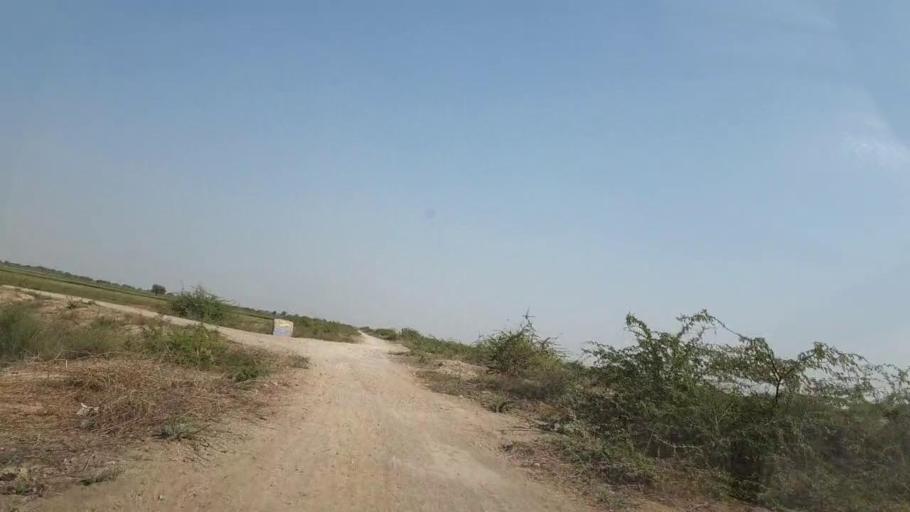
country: PK
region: Sindh
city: Nabisar
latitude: 25.0750
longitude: 69.5473
